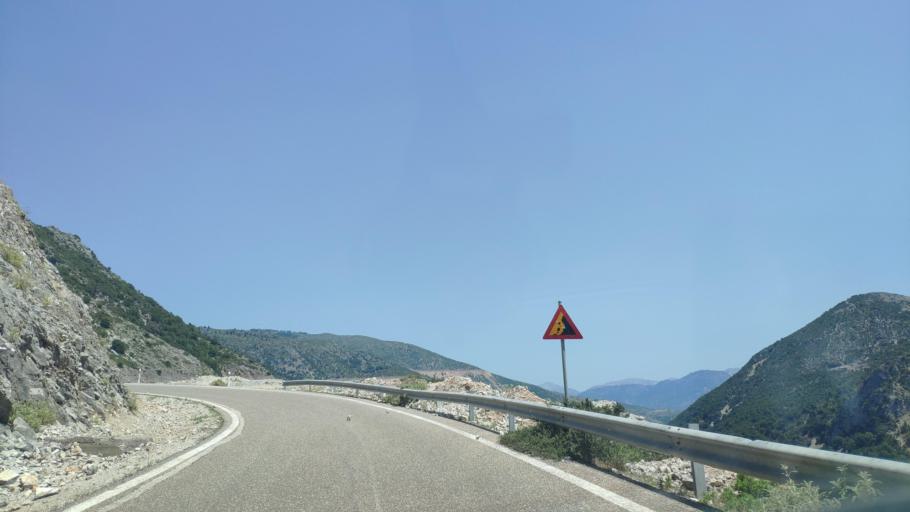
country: GR
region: West Greece
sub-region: Nomos Aitolias kai Akarnanias
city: Krikellos
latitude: 39.0152
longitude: 21.3708
